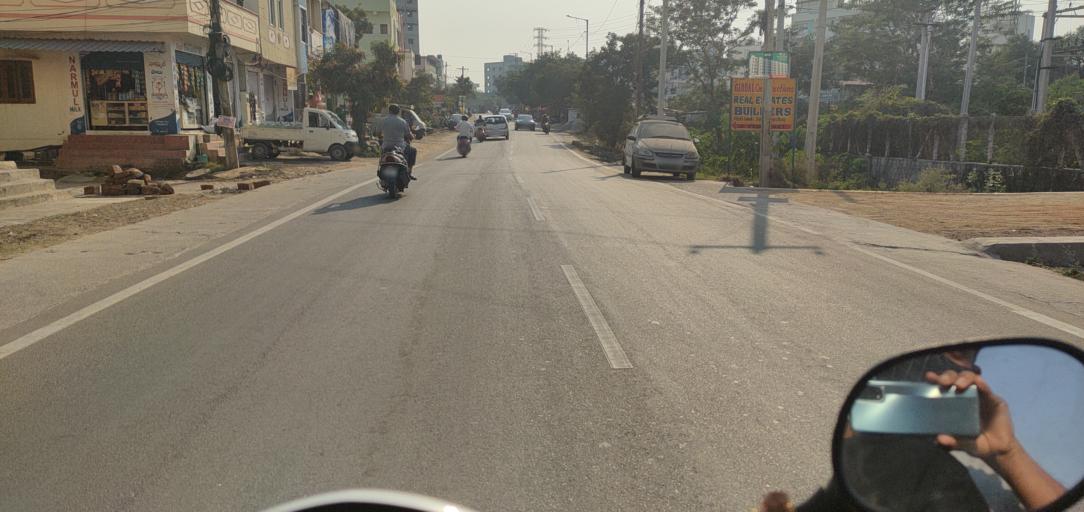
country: IN
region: Telangana
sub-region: Rangareddi
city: Lal Bahadur Nagar
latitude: 17.3346
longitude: 78.6130
